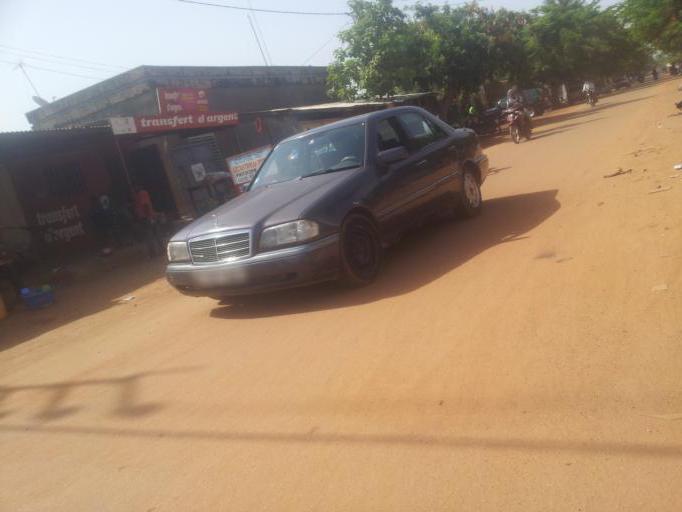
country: BF
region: Centre
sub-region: Kadiogo Province
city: Ouagadougou
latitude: 12.3786
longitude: -1.5372
